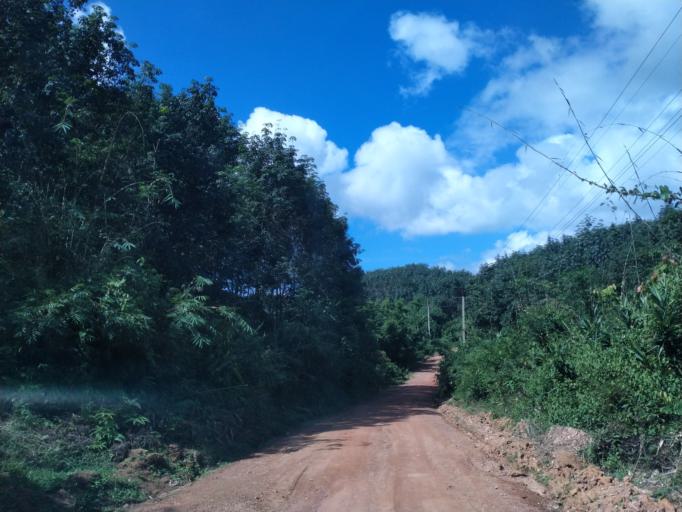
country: TH
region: Nong Khai
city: Rattanawapi
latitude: 18.6355
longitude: 102.9597
